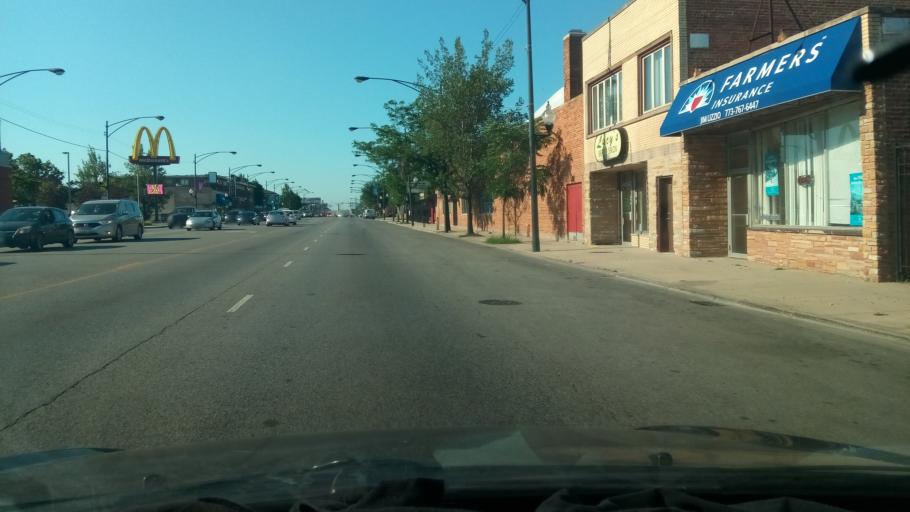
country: US
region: Illinois
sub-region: Cook County
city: Hometown
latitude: 41.7707
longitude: -87.7227
